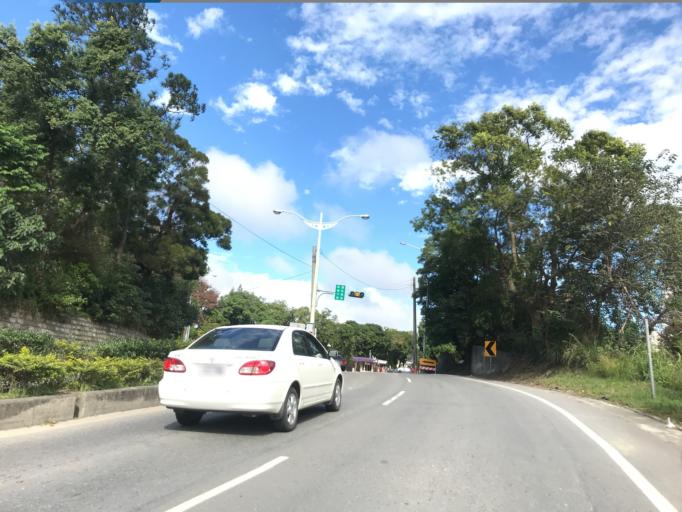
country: TW
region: Taiwan
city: Daxi
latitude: 24.8468
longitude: 121.2458
